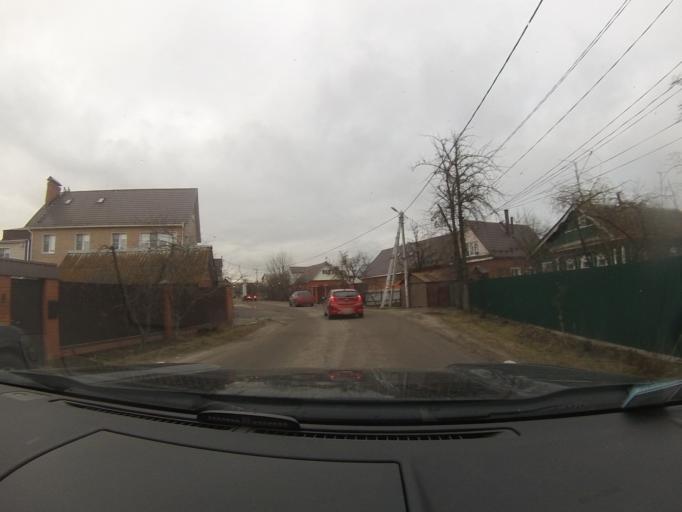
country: RU
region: Moskovskaya
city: Voskresensk
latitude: 55.3281
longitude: 38.6798
